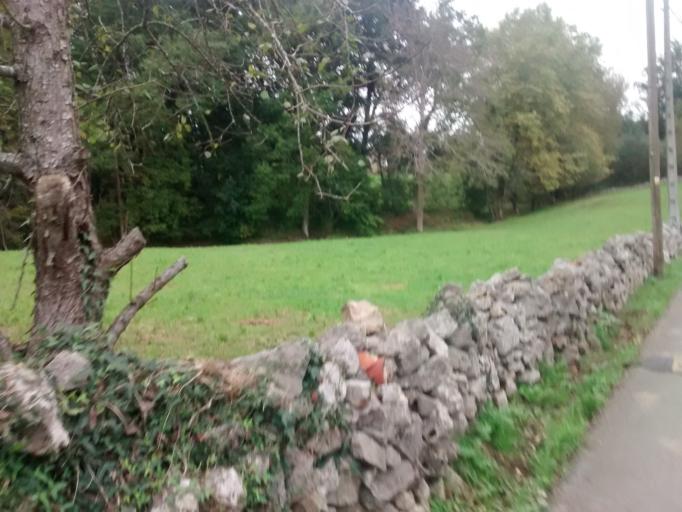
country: ES
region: Cantabria
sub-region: Provincia de Cantabria
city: Entrambasaguas
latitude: 43.3421
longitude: -3.6925
